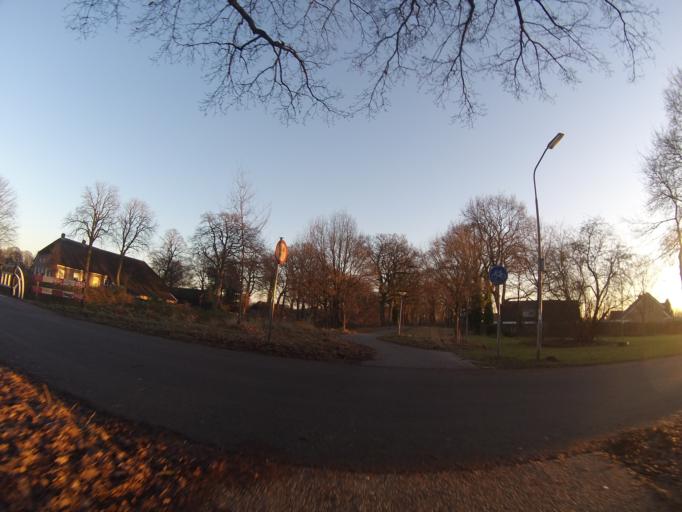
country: NL
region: Drenthe
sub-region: Gemeente Emmen
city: Emmen
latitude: 52.7535
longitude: 6.8967
